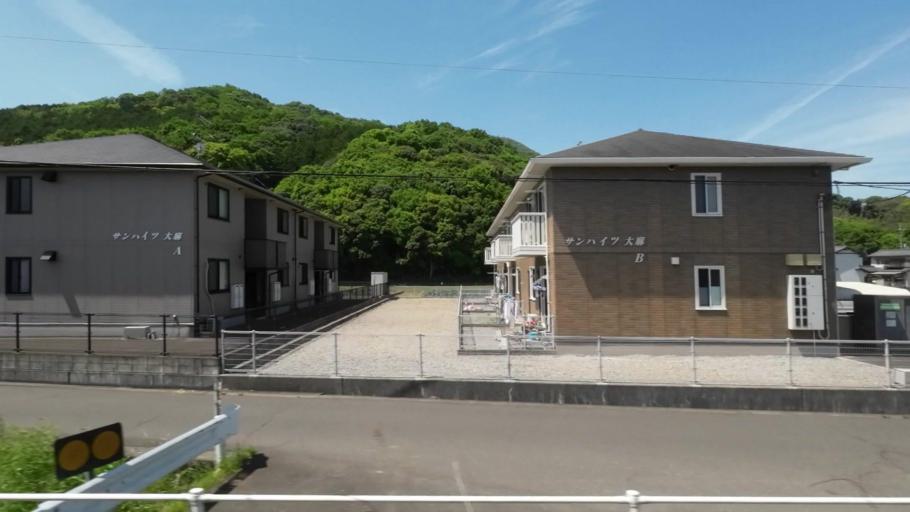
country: JP
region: Kagawa
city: Marugame
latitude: 34.2066
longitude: 133.8063
